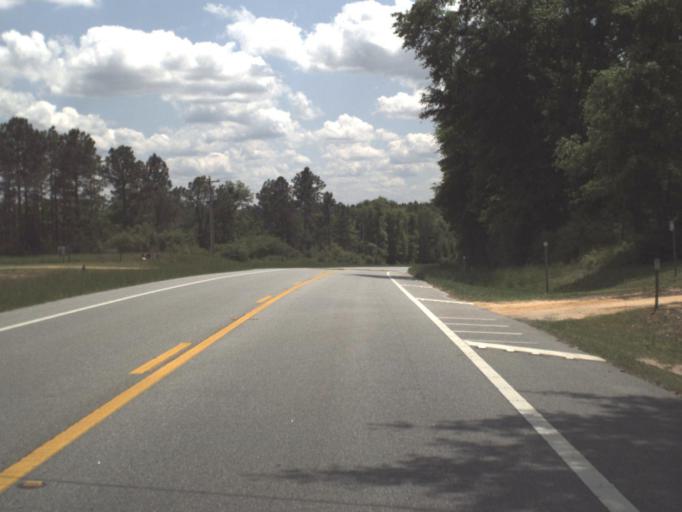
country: US
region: Alabama
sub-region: Escambia County
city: Atmore
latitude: 30.9117
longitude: -87.4793
